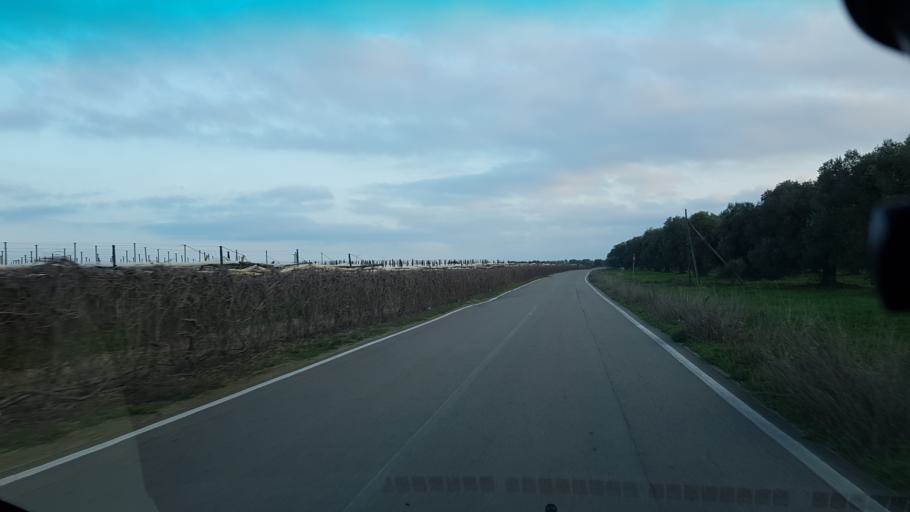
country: IT
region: Apulia
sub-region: Provincia di Brindisi
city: Mesagne
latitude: 40.6297
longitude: 17.7829
